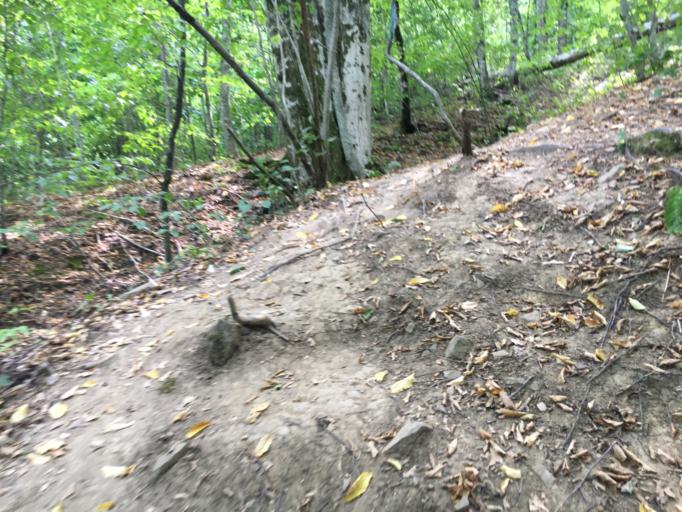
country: RU
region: Krasnodarskiy
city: Tuapse
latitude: 44.2551
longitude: 39.2257
